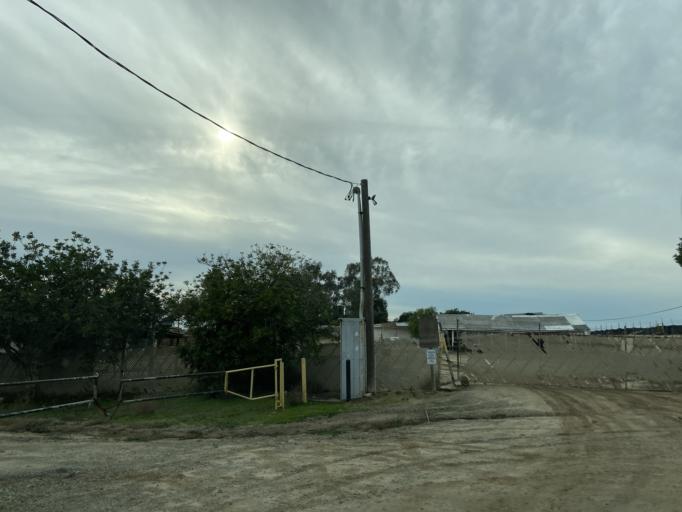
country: US
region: California
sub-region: San Diego County
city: Bonsall
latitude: 33.2596
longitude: -117.2794
